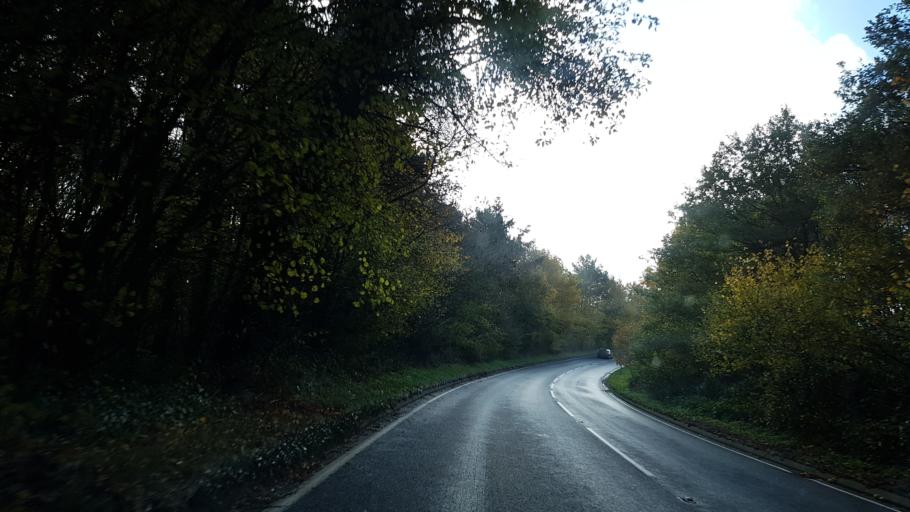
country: GB
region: England
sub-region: Surrey
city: Milford
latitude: 51.1293
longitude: -0.6723
